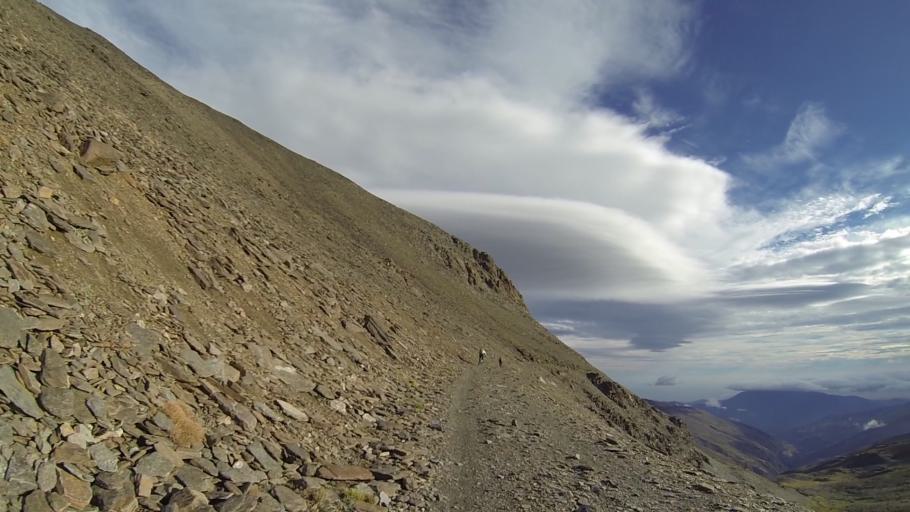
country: ES
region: Andalusia
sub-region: Provincia de Granada
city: Trevelez
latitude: 37.0499
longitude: -3.3207
